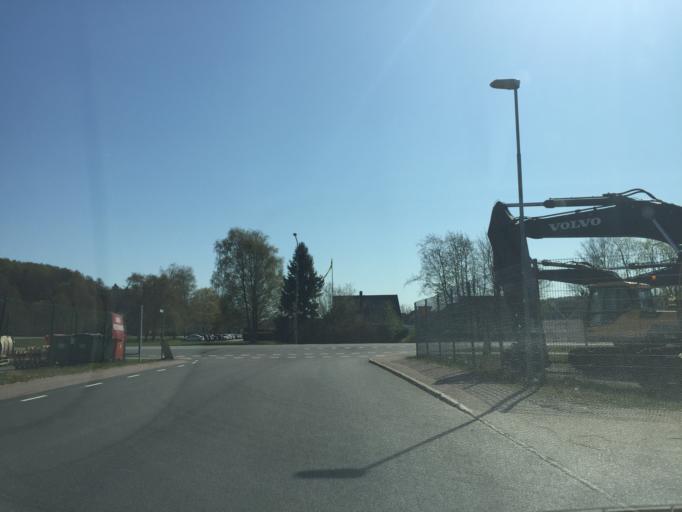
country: SE
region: Vaestra Goetaland
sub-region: Kungalvs Kommun
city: Kungalv
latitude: 57.8853
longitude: 11.9885
